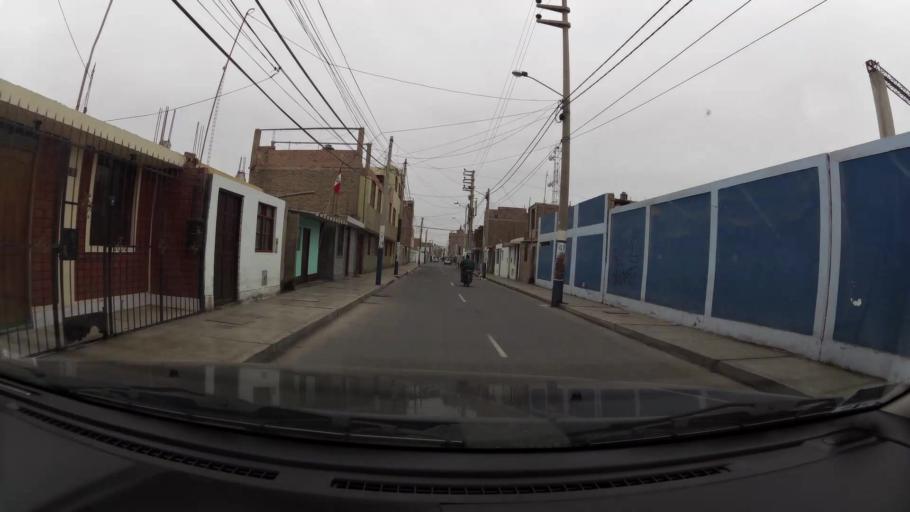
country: PE
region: Ica
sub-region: Provincia de Pisco
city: Pisco
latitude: -13.7088
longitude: -76.2001
